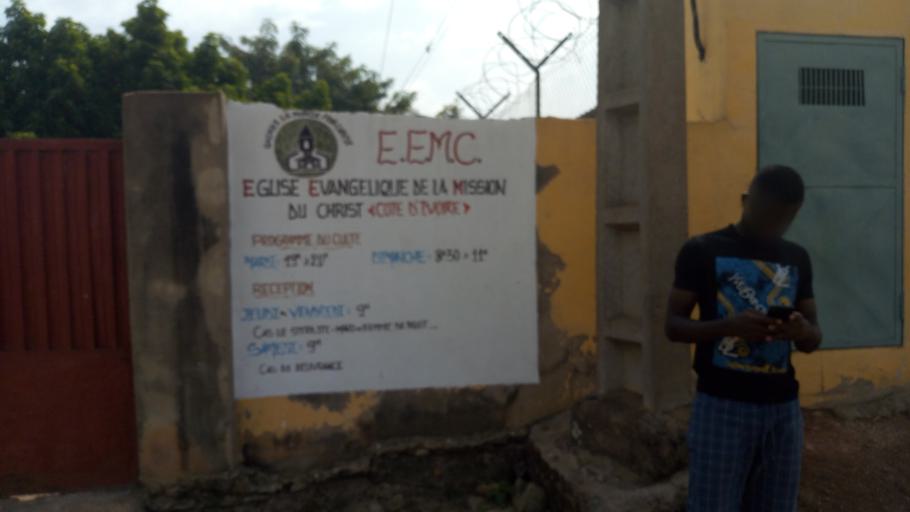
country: CI
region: Vallee du Bandama
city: Bouake
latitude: 7.6775
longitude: -5.0597
